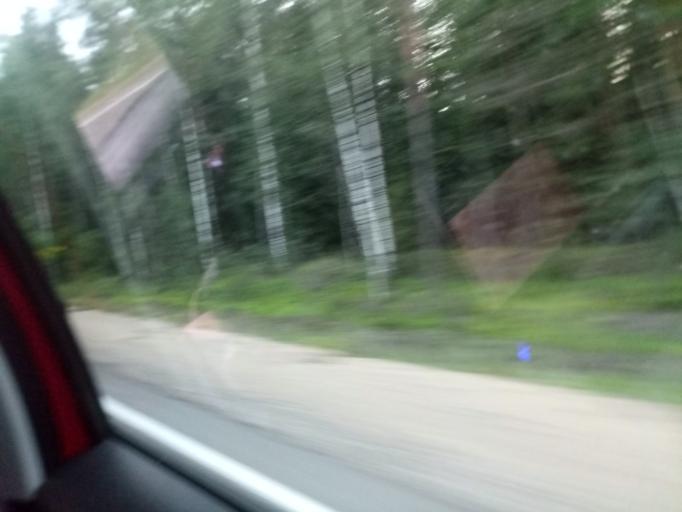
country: RU
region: Moskovskaya
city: Noginsk-9
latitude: 56.0888
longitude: 38.5790
